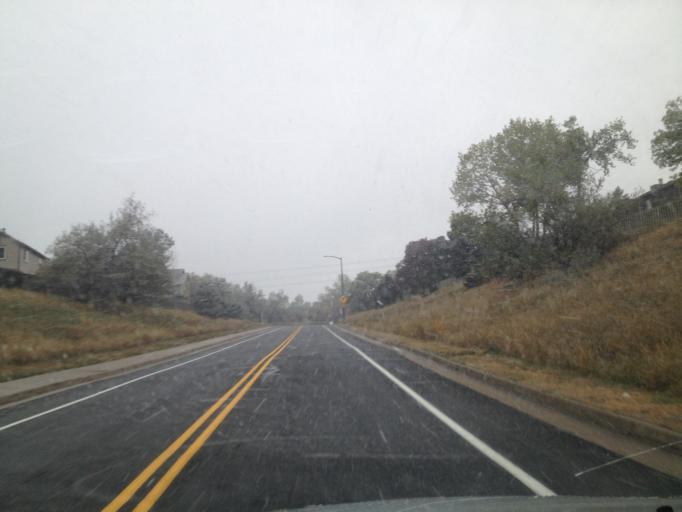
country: US
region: Colorado
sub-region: Boulder County
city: Louisville
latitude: 39.9792
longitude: -105.1538
